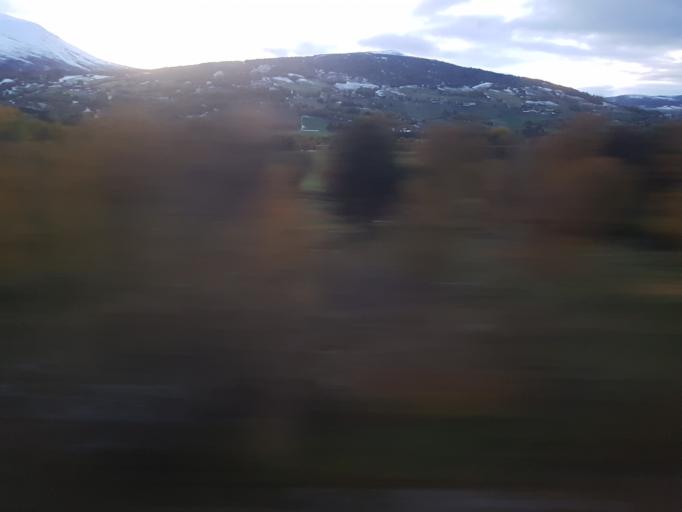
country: NO
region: Sor-Trondelag
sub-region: Oppdal
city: Oppdal
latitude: 62.5850
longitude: 9.6575
